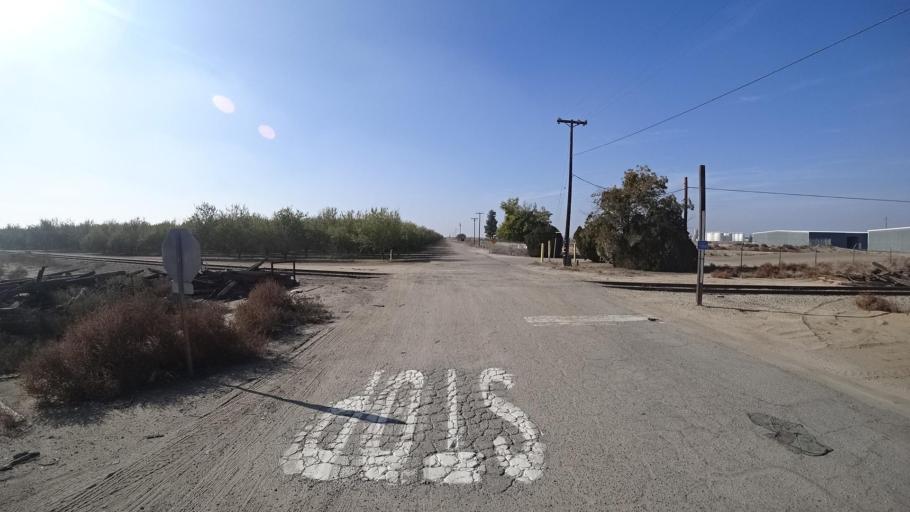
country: US
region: California
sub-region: Kern County
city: McFarland
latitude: 35.6310
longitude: -119.2069
